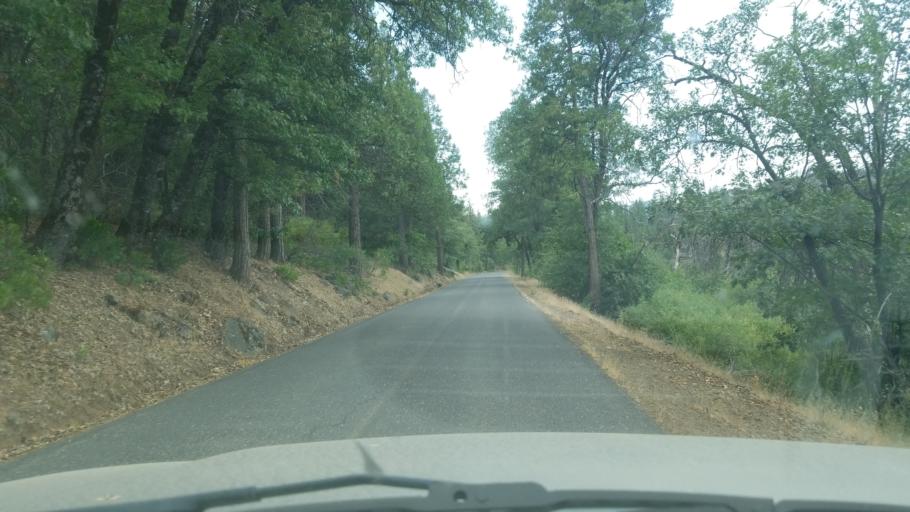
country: US
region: California
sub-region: Mariposa County
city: Yosemite Valley
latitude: 37.8909
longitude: -119.8479
